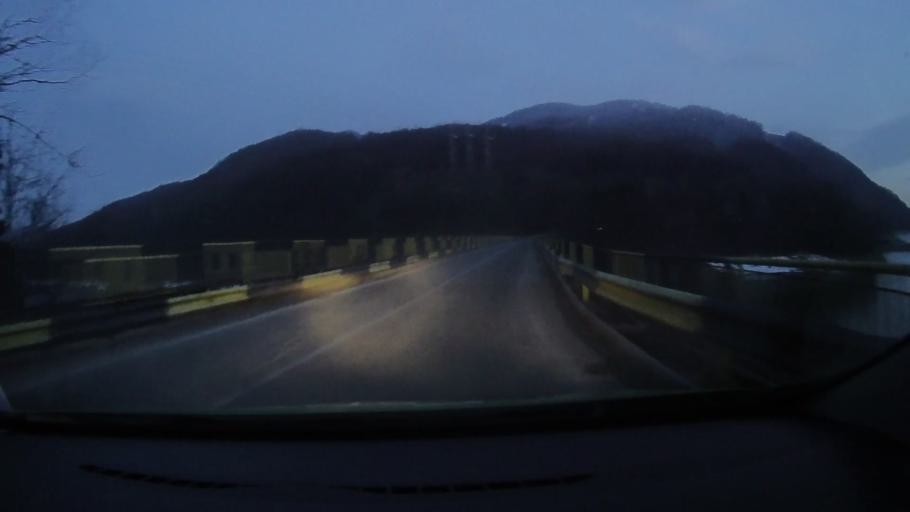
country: RO
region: Prahova
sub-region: Comuna Sotrile
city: Sotrile
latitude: 45.2549
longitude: 25.7415
